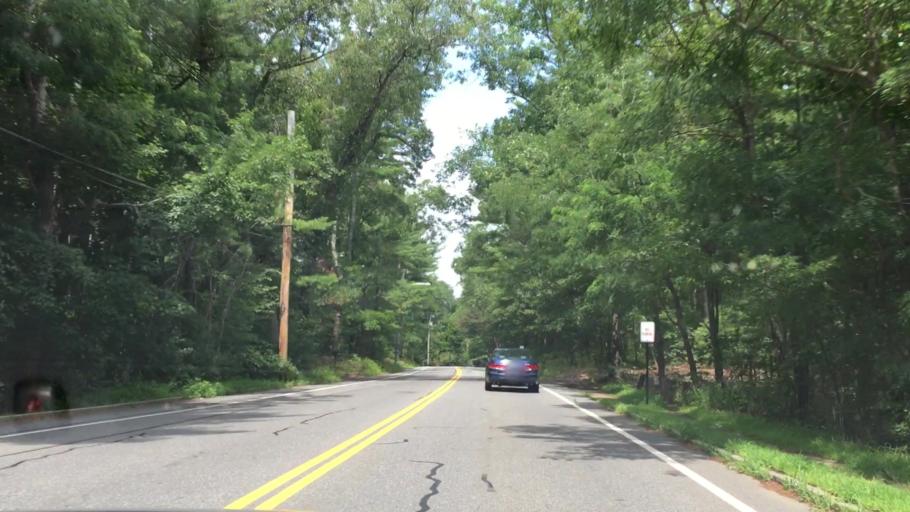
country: US
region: Massachusetts
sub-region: Middlesex County
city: Concord
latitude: 42.4453
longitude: -71.3407
